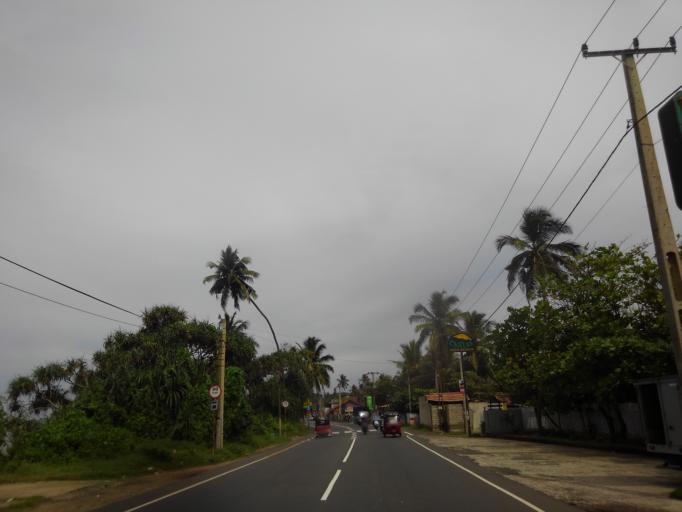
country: LK
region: Western
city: Beruwala
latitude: 6.4829
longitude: 79.9834
